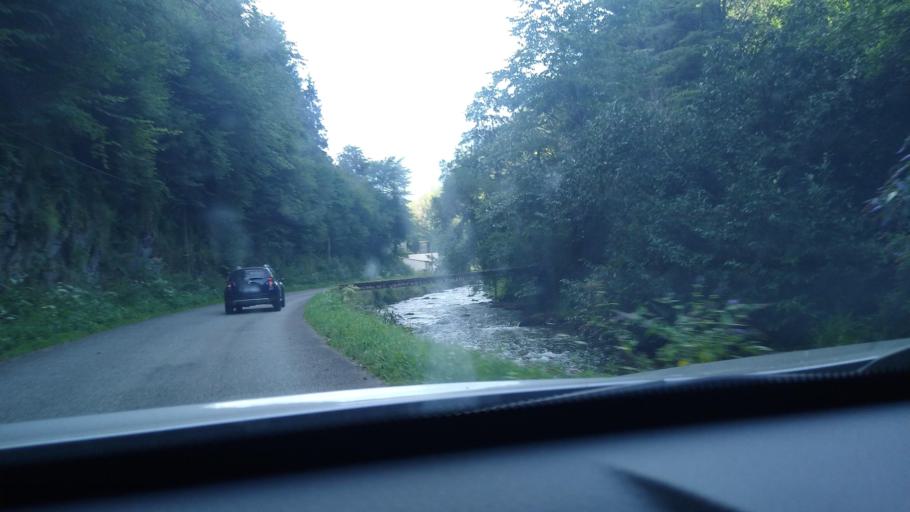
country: FR
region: Midi-Pyrenees
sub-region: Departement de l'Ariege
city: Saint-Girons
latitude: 42.8108
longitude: 1.1973
